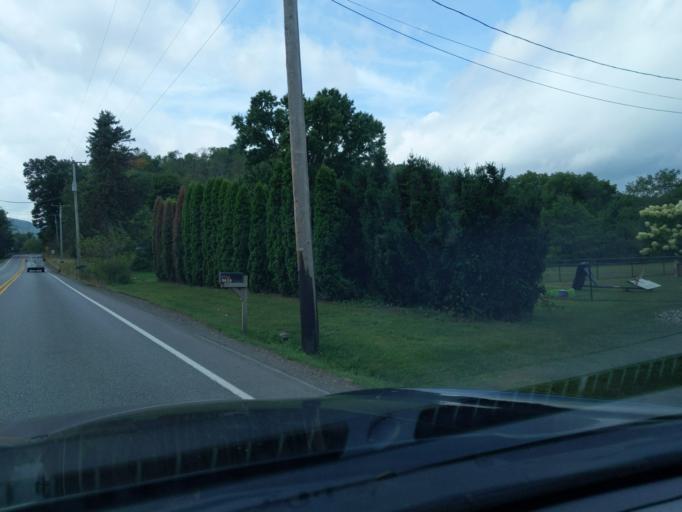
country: US
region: Pennsylvania
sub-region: Blair County
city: Duncansville
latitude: 40.3870
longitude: -78.4130
